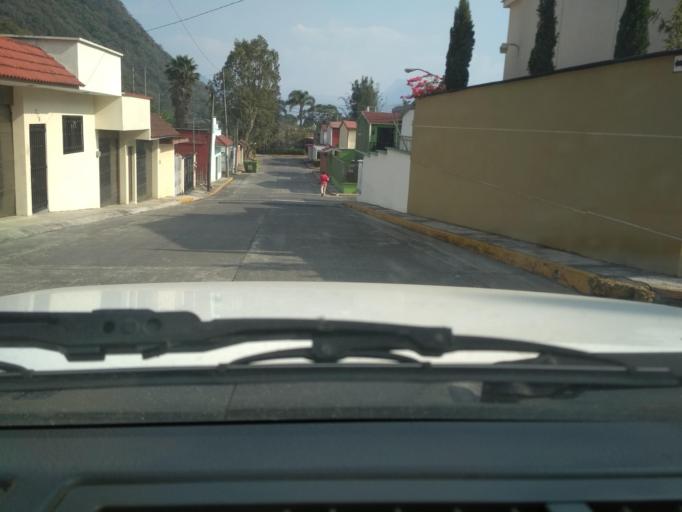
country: MX
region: Veracruz
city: Orizaba
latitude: 18.8667
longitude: -97.0947
